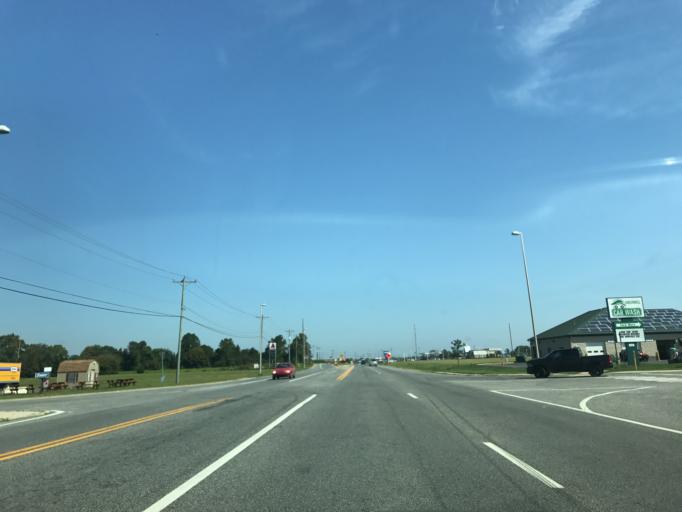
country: US
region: Delaware
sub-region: New Castle County
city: Middletown
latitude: 39.4379
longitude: -75.7522
